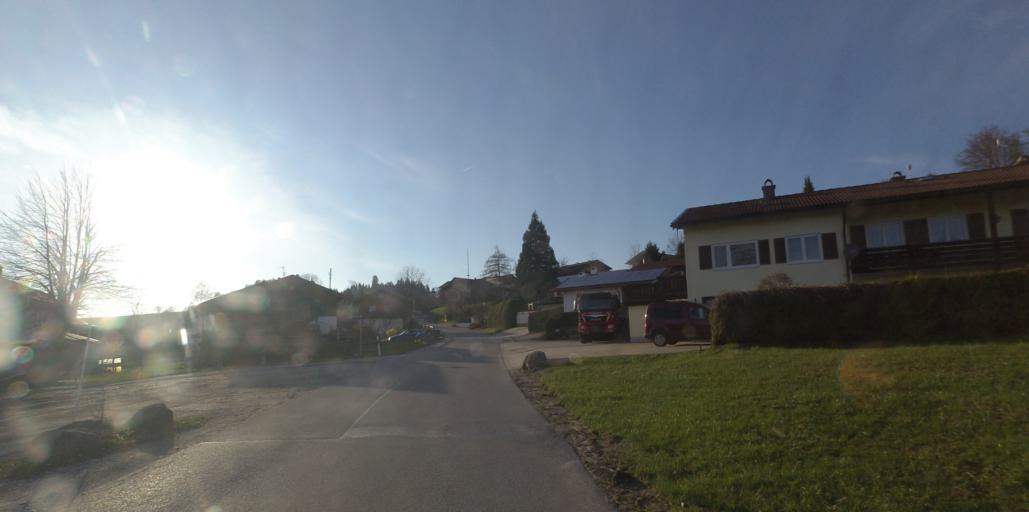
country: DE
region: Bavaria
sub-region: Upper Bavaria
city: Bergen
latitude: 47.8294
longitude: 12.5753
